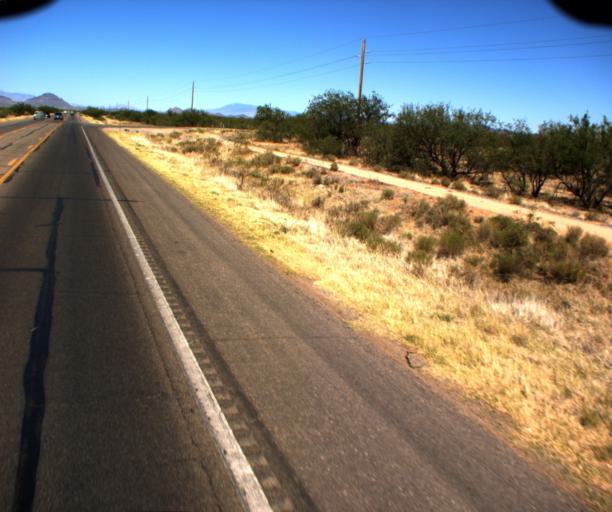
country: US
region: Arizona
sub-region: Pima County
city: Three Points
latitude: 32.1111
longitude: -111.2272
